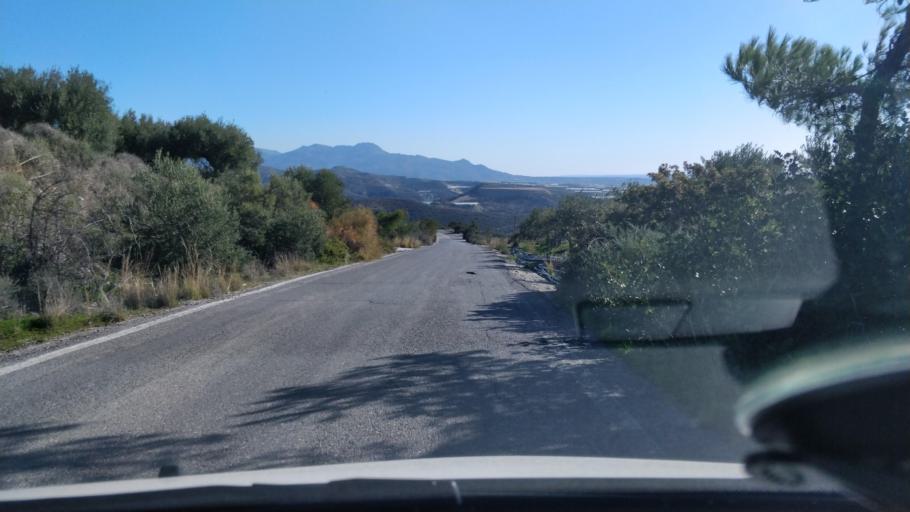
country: GR
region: Crete
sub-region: Nomos Lasithiou
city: Gra Liyia
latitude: 35.0370
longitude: 25.6654
